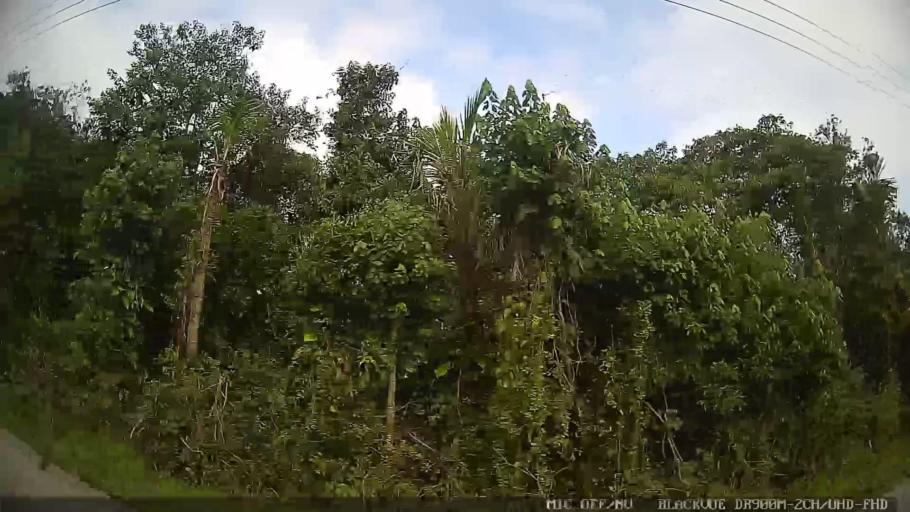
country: BR
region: Sao Paulo
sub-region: Guaruja
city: Guaruja
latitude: -23.9732
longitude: -46.2184
